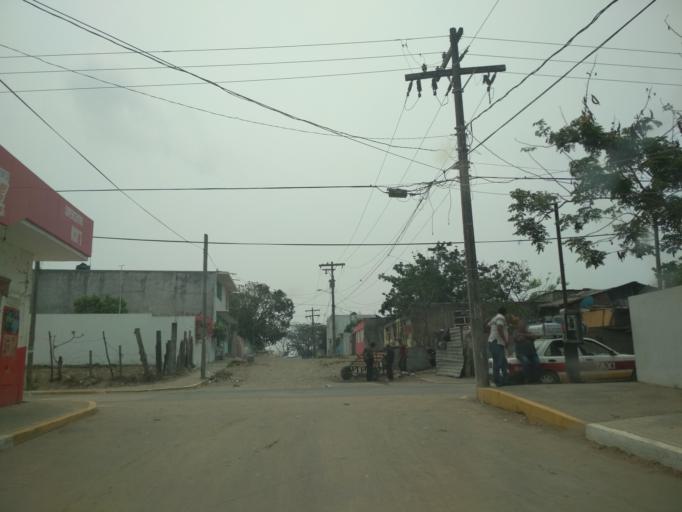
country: MX
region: Veracruz
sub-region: Veracruz
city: Rio Medio [Granja]
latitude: 19.2103
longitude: -96.2092
